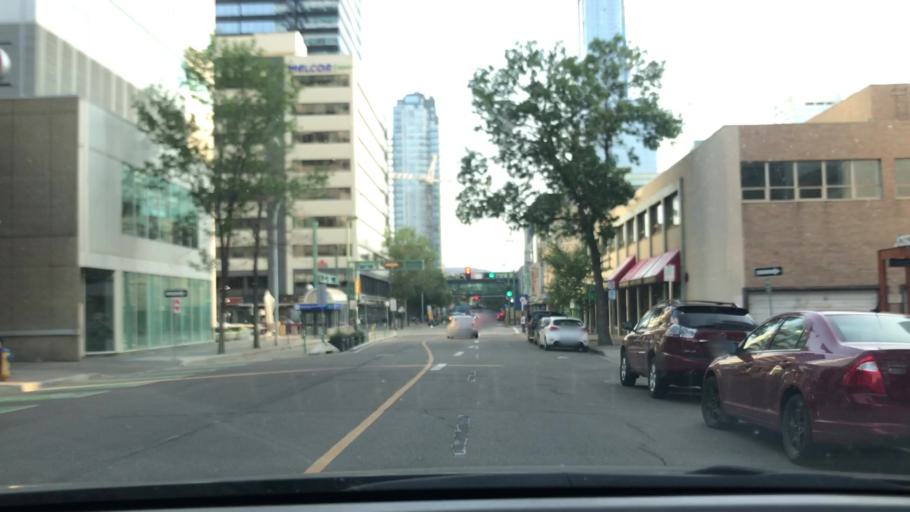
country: CA
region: Alberta
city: Edmonton
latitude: 53.5401
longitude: -113.4974
